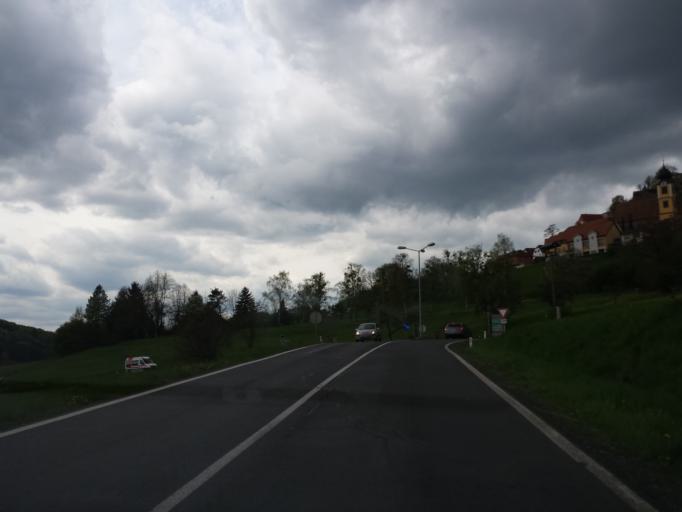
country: AT
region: Styria
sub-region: Politischer Bezirk Suedoststeiermark
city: Riegersburg
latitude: 46.9984
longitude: 15.9360
